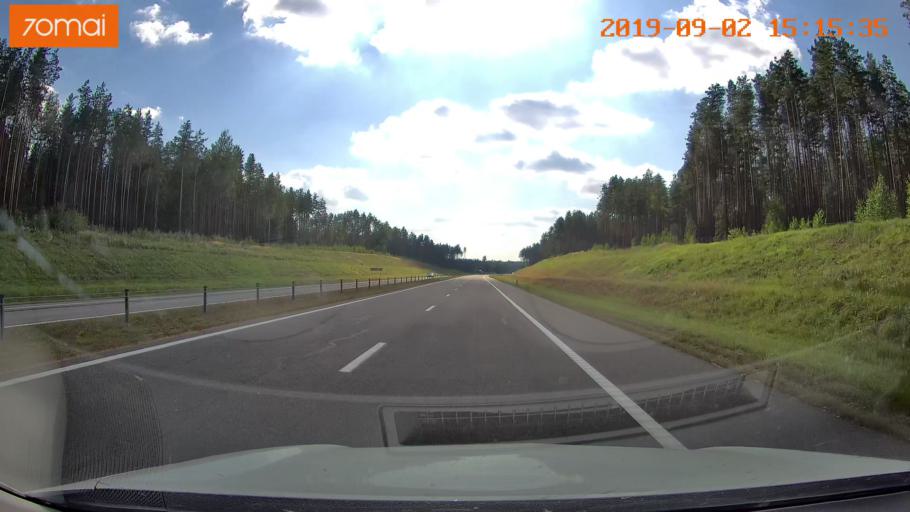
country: BY
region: Mogilev
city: Byalynichy
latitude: 53.9495
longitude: 29.6449
